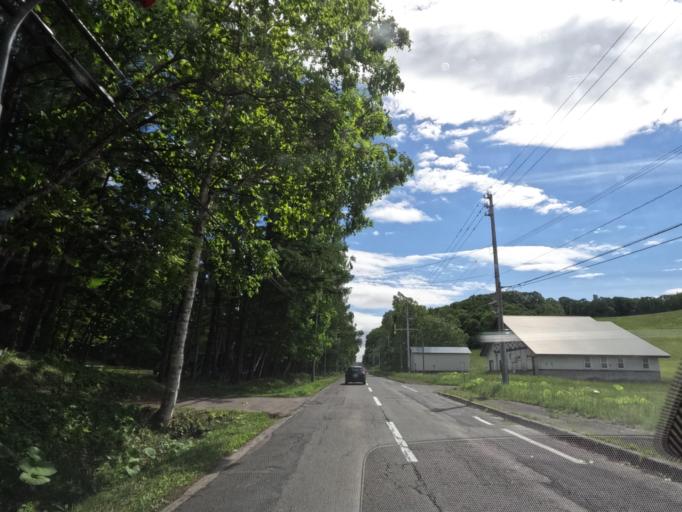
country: JP
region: Hokkaido
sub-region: Asahikawa-shi
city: Asahikawa
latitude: 43.8366
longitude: 142.5391
